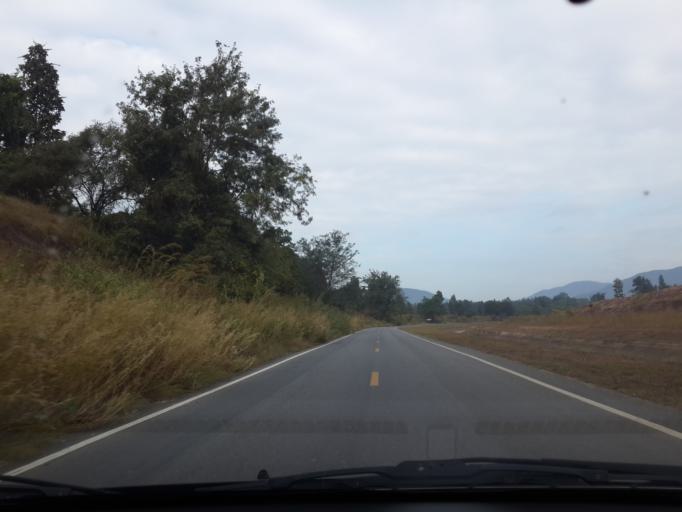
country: TH
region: Chiang Mai
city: San Sai
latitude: 18.8956
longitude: 99.1495
